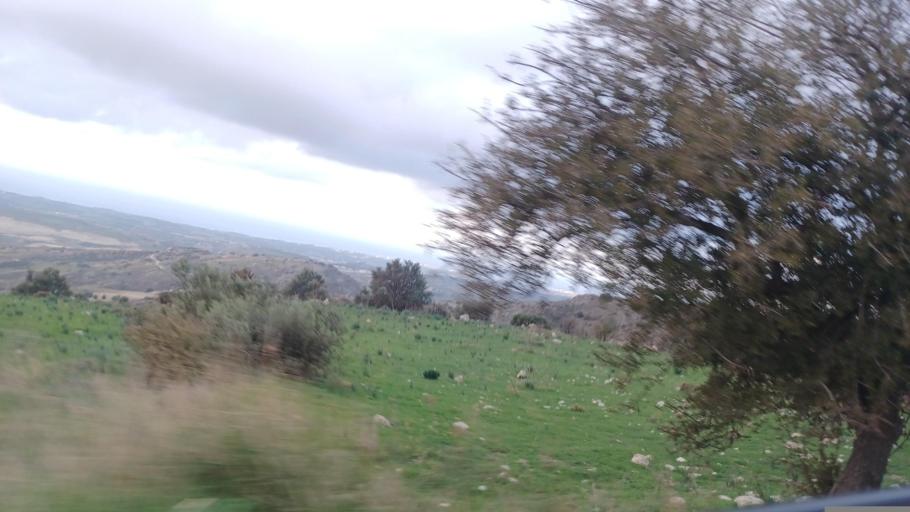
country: CY
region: Pafos
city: Mesogi
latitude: 34.7819
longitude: 32.5014
